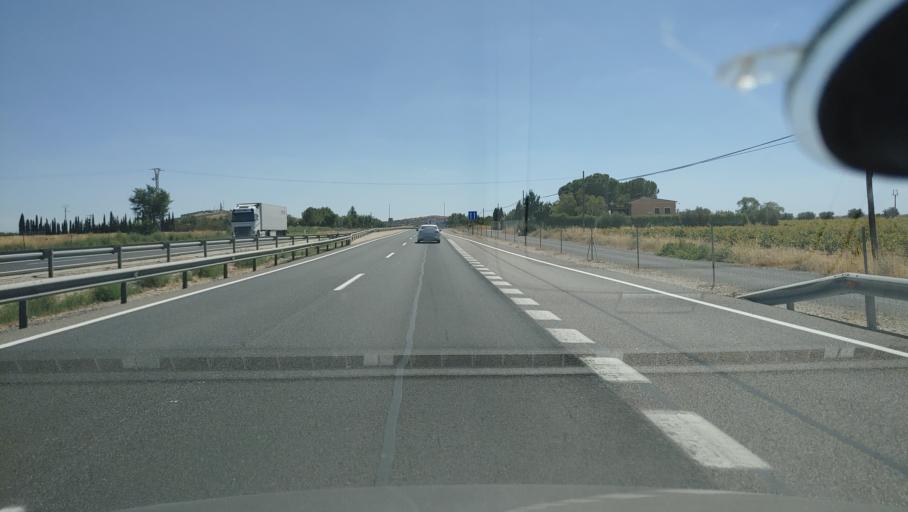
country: ES
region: Castille-La Mancha
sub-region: Provincia de Ciudad Real
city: Valdepenas
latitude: 38.8186
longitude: -3.3959
